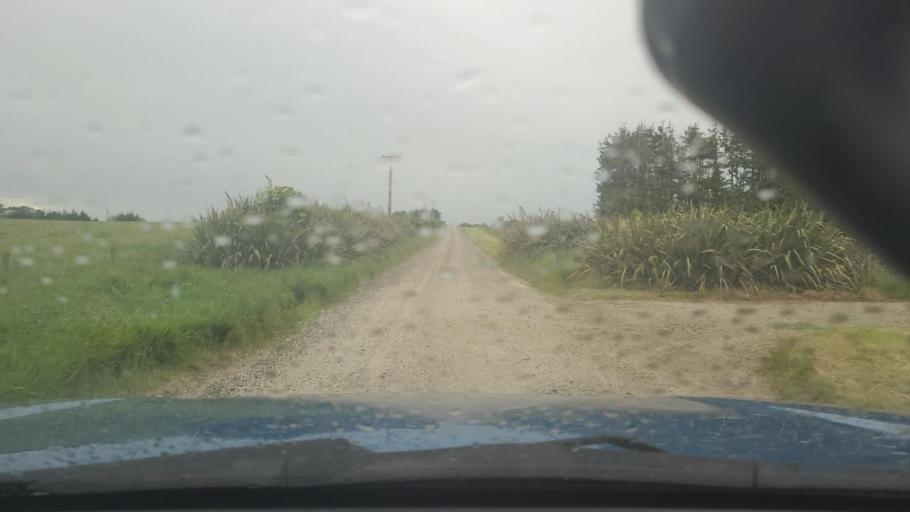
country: NZ
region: Southland
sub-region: Invercargill City
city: Invercargill
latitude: -46.3934
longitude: 168.5587
